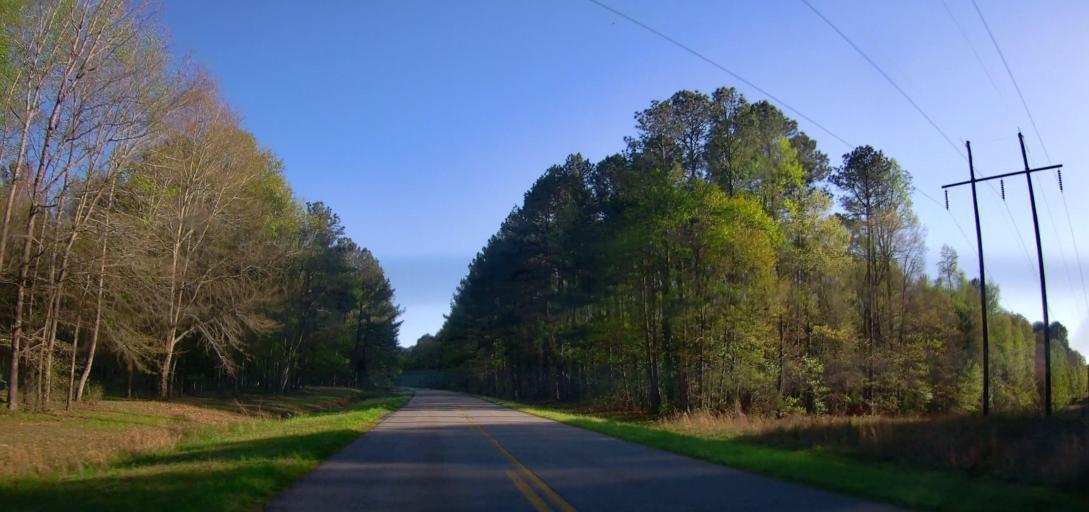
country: US
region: Georgia
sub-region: Butts County
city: Indian Springs
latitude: 33.2958
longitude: -83.8966
